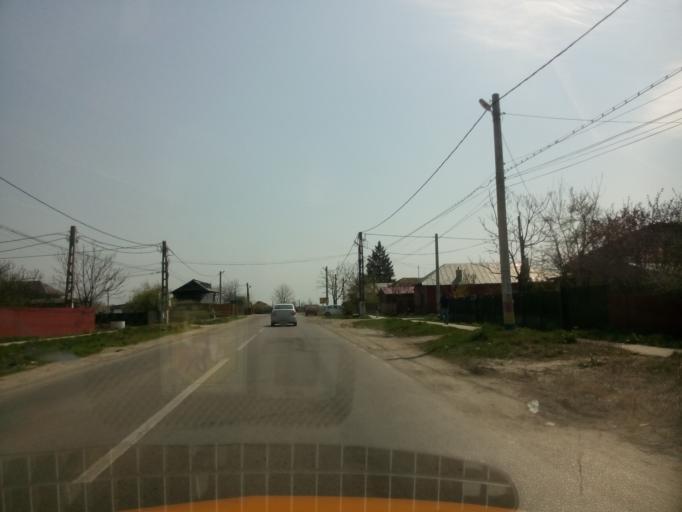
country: RO
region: Calarasi
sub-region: Comuna Soldanu
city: Soldanu
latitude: 44.2214
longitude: 26.5273
